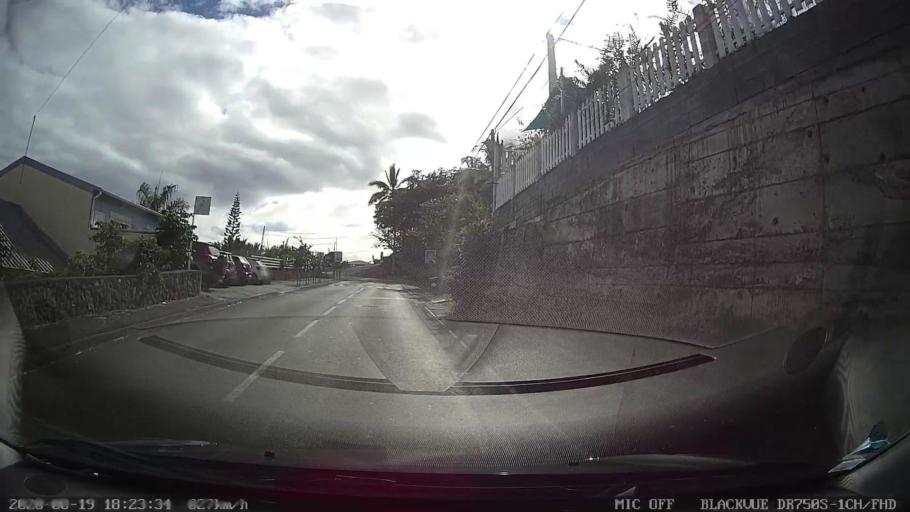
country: RE
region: Reunion
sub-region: Reunion
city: La Possession
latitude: -20.9522
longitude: 55.3424
